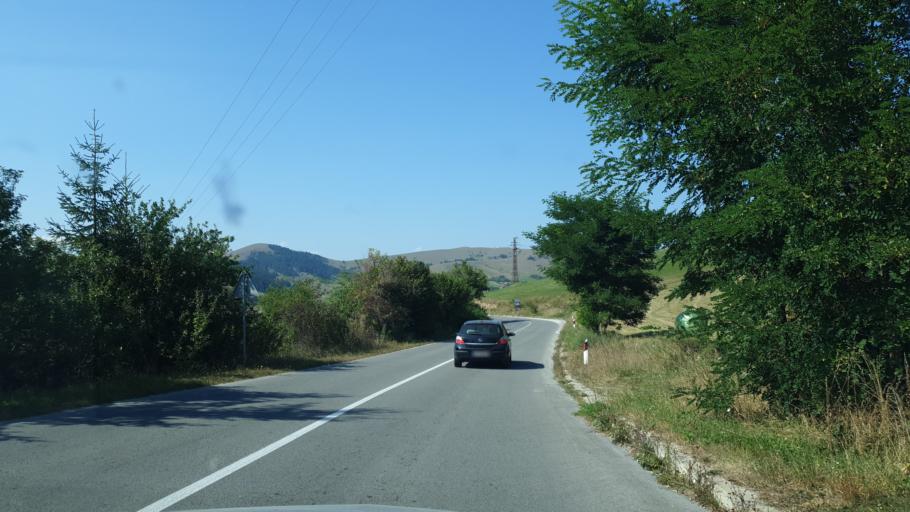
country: RS
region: Central Serbia
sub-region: Zlatiborski Okrug
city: Cajetina
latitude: 43.7144
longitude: 19.7635
